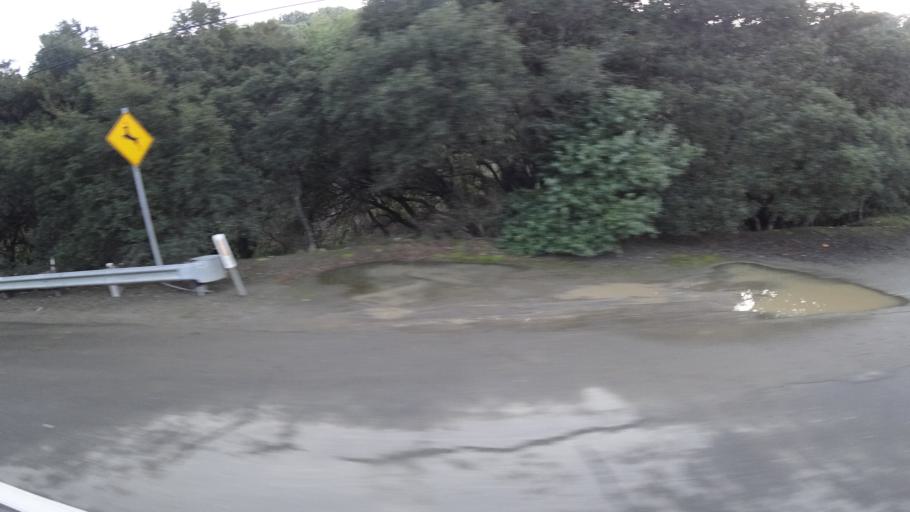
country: US
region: California
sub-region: Alameda County
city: Fairview
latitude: 37.7000
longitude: -122.0321
